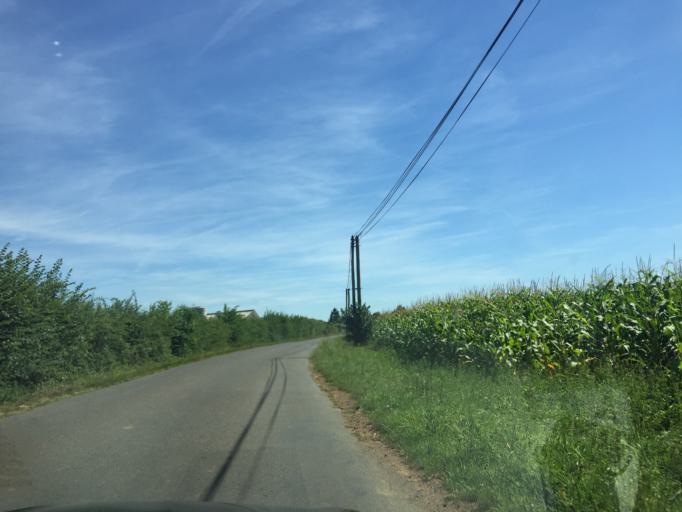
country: FR
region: Poitou-Charentes
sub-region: Departement de la Vienne
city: La Villedieu-du-Clain
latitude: 46.4407
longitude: 0.3268
